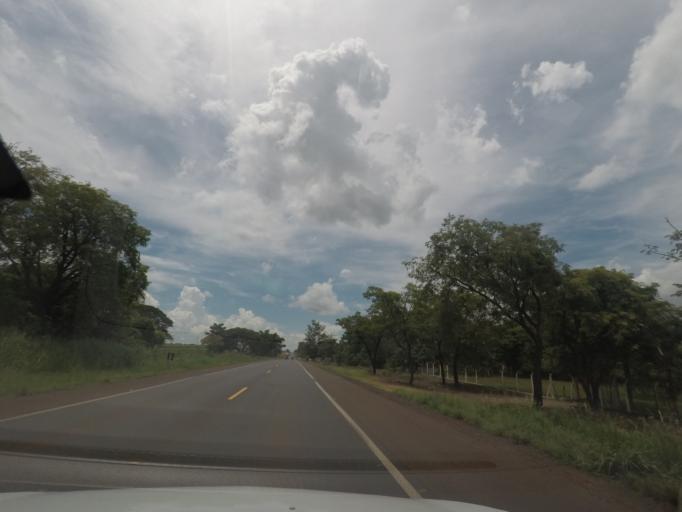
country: BR
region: Sao Paulo
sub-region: Barretos
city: Barretos
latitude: -20.3681
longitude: -48.6464
